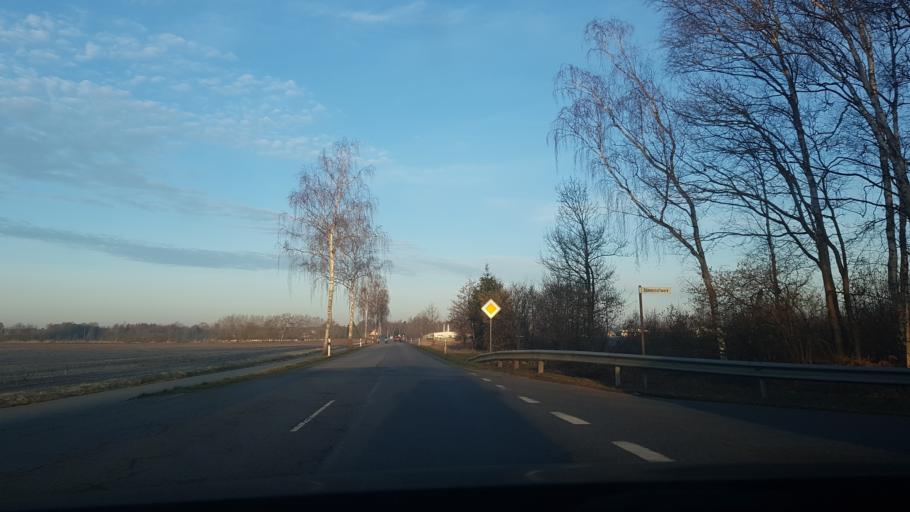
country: DE
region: Lower Saxony
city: Sassenburg
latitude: 52.5054
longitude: 10.6002
